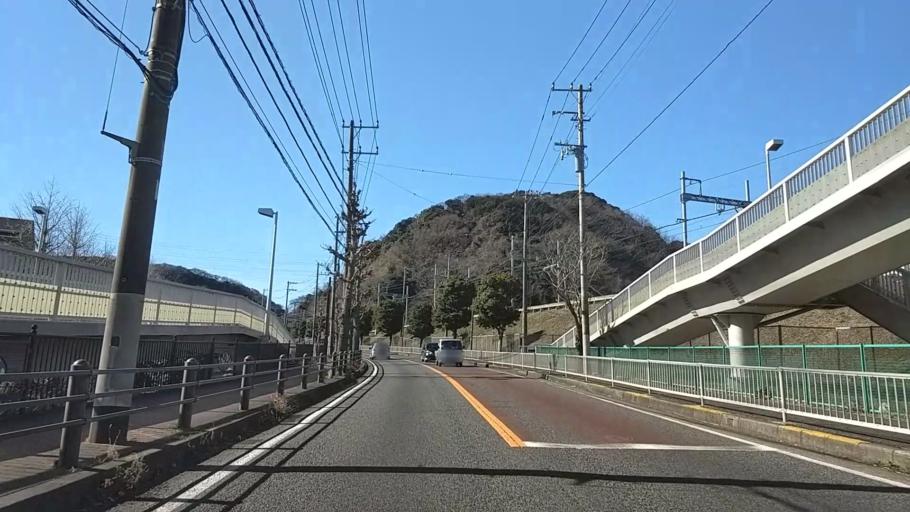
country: JP
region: Kanagawa
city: Yokosuka
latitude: 35.2258
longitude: 139.7001
